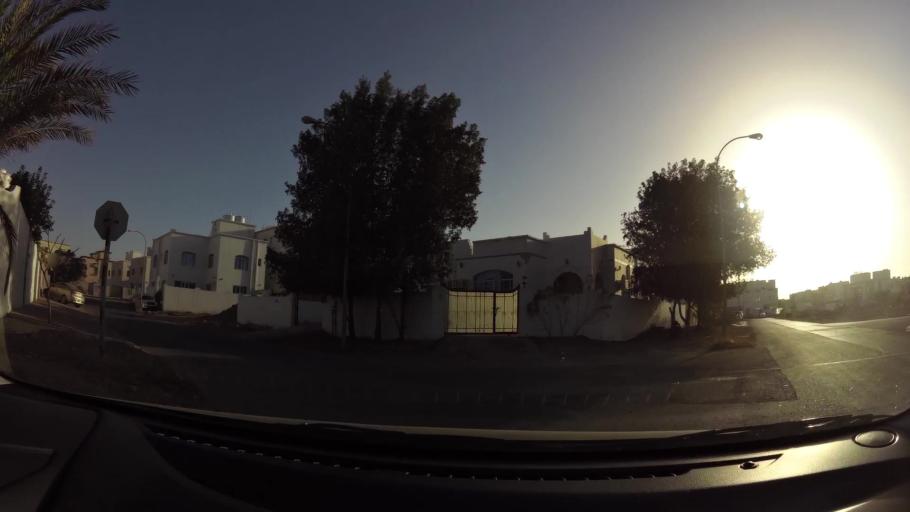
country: OM
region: Muhafazat Masqat
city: As Sib al Jadidah
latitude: 23.6094
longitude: 58.2326
